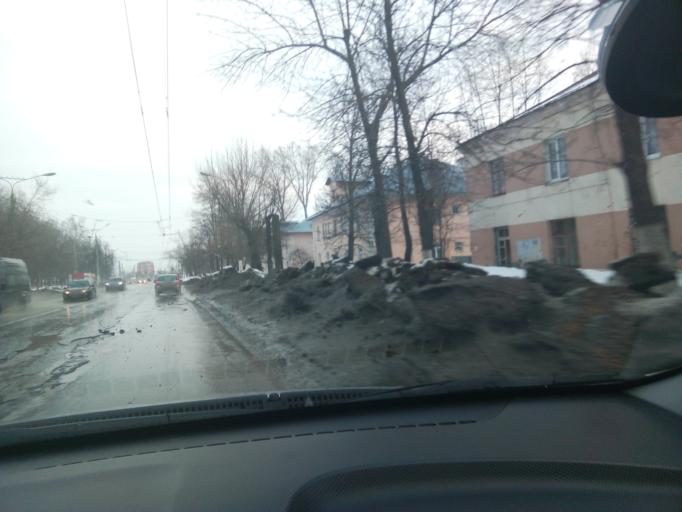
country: RU
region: Chuvashia
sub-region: Cheboksarskiy Rayon
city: Cheboksary
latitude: 56.1258
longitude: 47.2086
